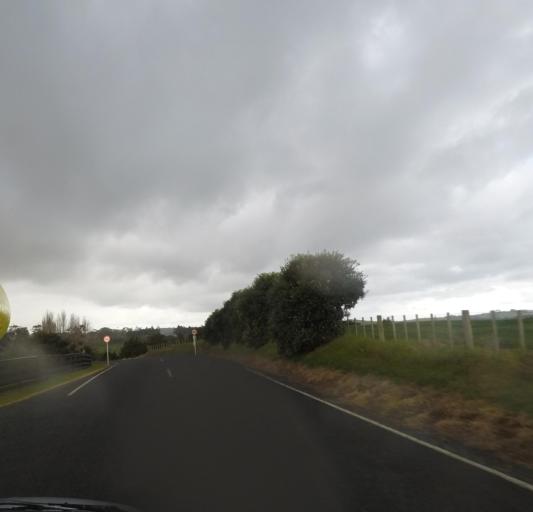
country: NZ
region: Auckland
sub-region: Auckland
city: Warkworth
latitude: -36.3757
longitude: 174.7601
